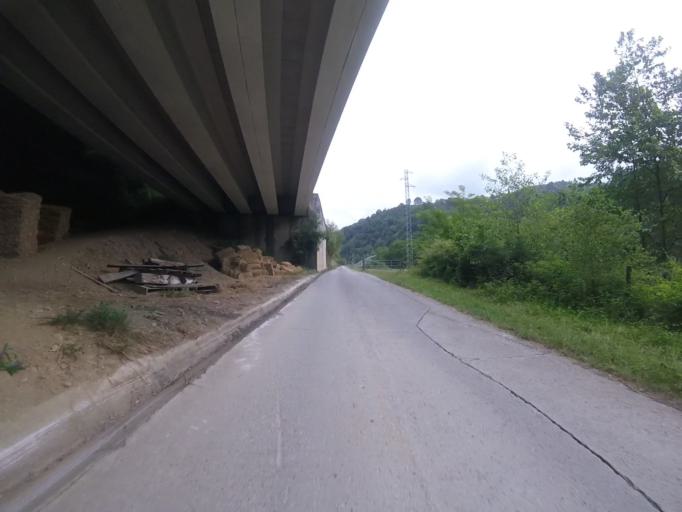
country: ES
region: Navarre
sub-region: Provincia de Navarra
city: Sunbilla
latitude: 43.1813
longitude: -1.6708
